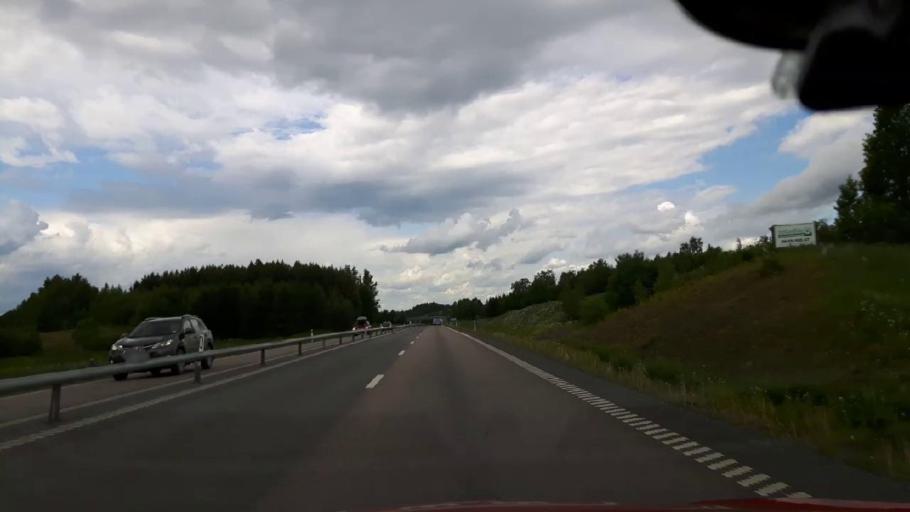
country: SE
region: Jaemtland
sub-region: Krokoms Kommun
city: Krokom
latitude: 63.3009
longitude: 14.4947
